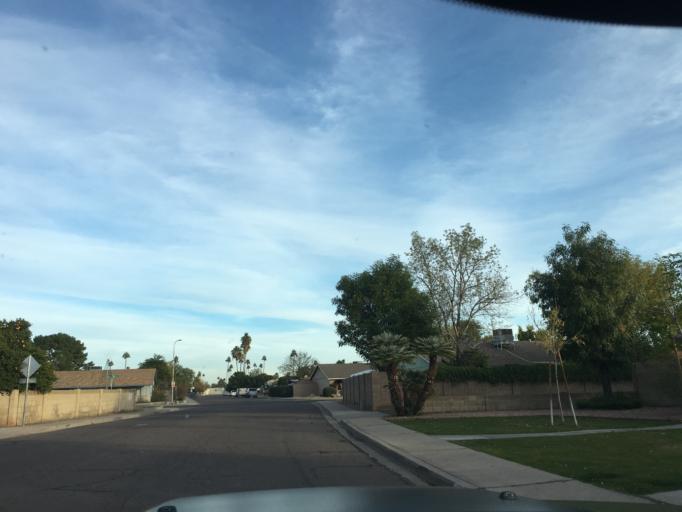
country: US
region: Arizona
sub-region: Maricopa County
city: Tempe
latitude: 33.3748
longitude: -111.9056
